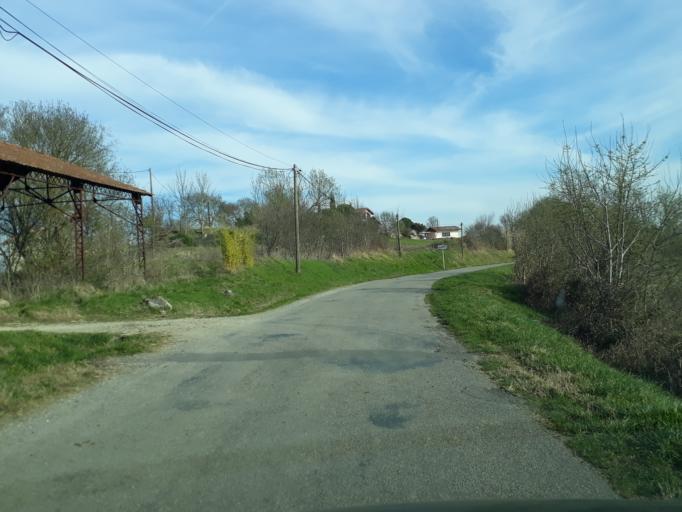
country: FR
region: Midi-Pyrenees
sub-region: Departement de la Haute-Garonne
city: Montesquieu-Volvestre
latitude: 43.1815
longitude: 1.3125
